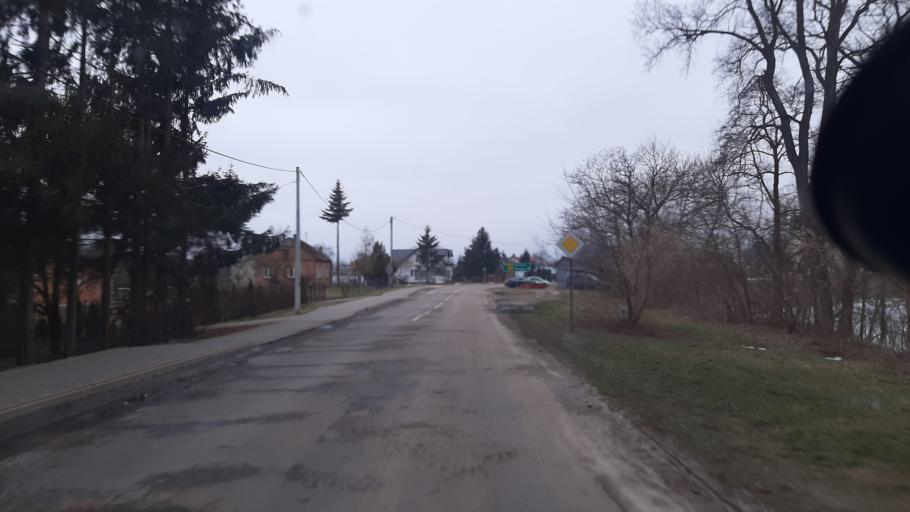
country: PL
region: Lublin Voivodeship
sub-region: Powiat wlodawski
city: Wlodawa
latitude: 51.5232
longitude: 23.5744
